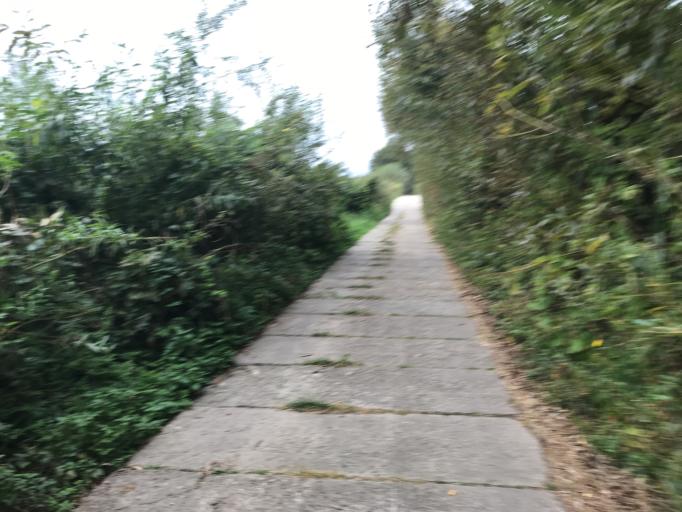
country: PL
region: Podlasie
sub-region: Powiat bialostocki
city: Choroszcz
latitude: 53.1386
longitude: 22.8719
